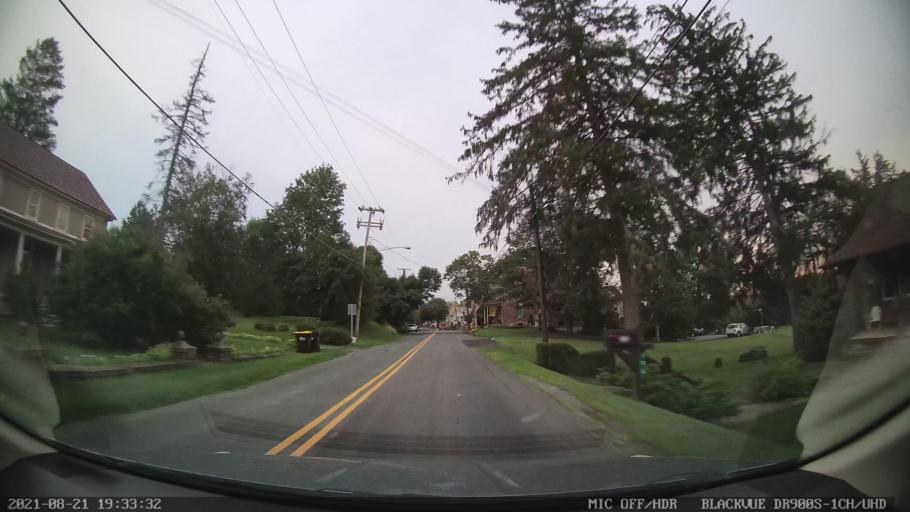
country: US
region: Pennsylvania
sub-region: Berks County
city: Oley
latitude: 40.3919
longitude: -75.7947
